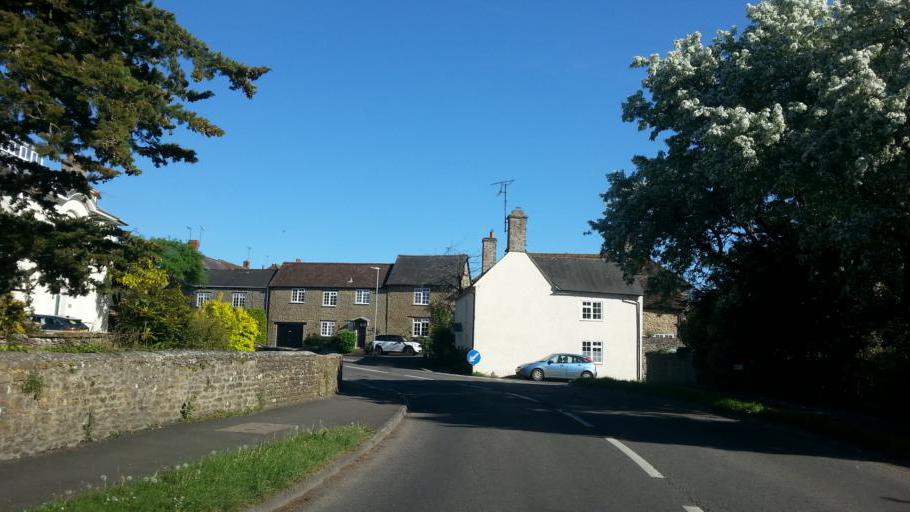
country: GB
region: England
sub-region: Dorset
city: Stalbridge
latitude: 50.9776
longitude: -2.3953
